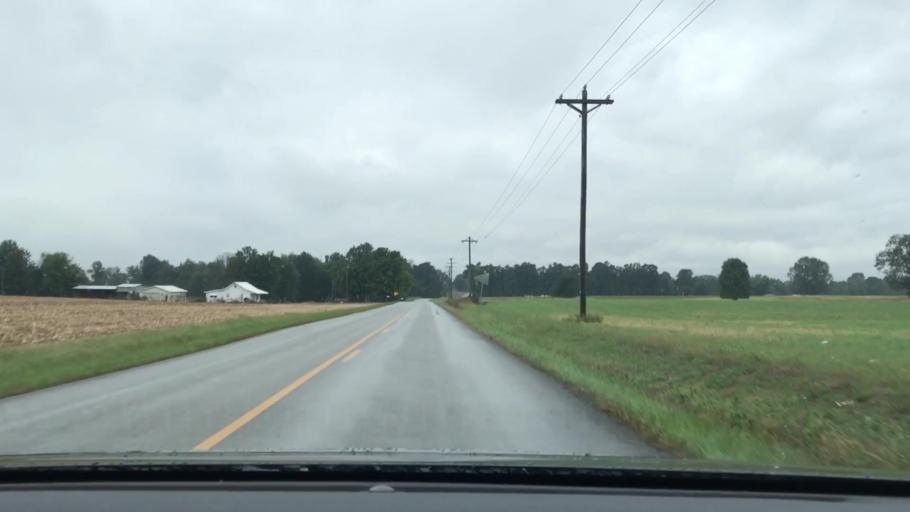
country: US
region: Kentucky
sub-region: McLean County
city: Calhoun
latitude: 37.4031
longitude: -87.2664
